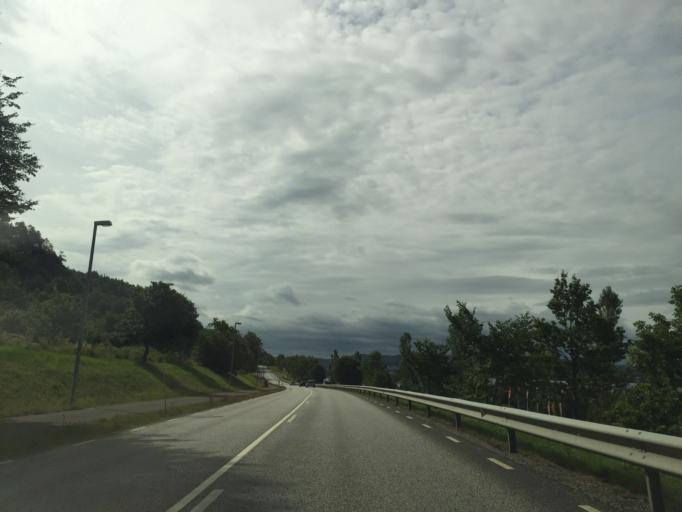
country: SE
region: Joenkoeping
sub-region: Jonkopings Kommun
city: Huskvarna
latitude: 57.8242
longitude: 14.2705
